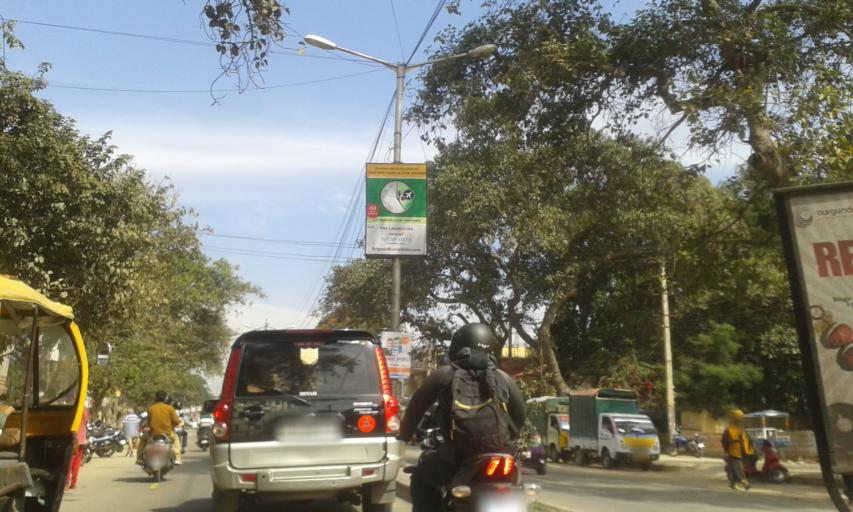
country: IN
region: Karnataka
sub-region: Bangalore Rural
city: Hoskote
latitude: 12.9679
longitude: 77.7496
